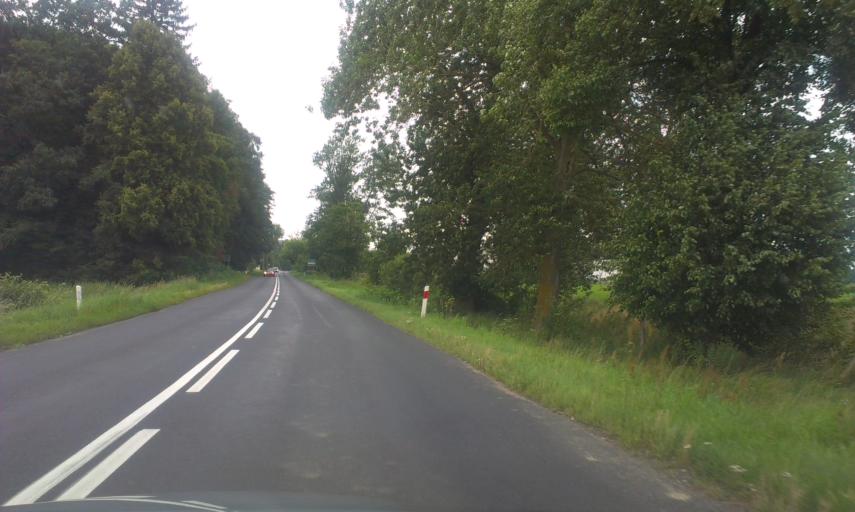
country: PL
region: West Pomeranian Voivodeship
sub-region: Powiat swidwinski
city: Rabino
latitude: 53.8888
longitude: 16.0693
